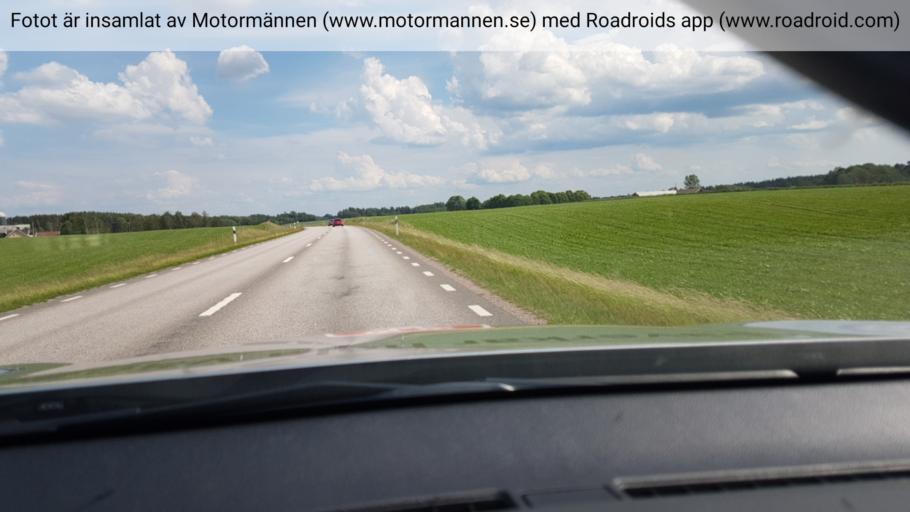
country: SE
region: Vaestra Goetaland
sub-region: Tibro Kommun
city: Tibro
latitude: 58.3500
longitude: 14.0890
